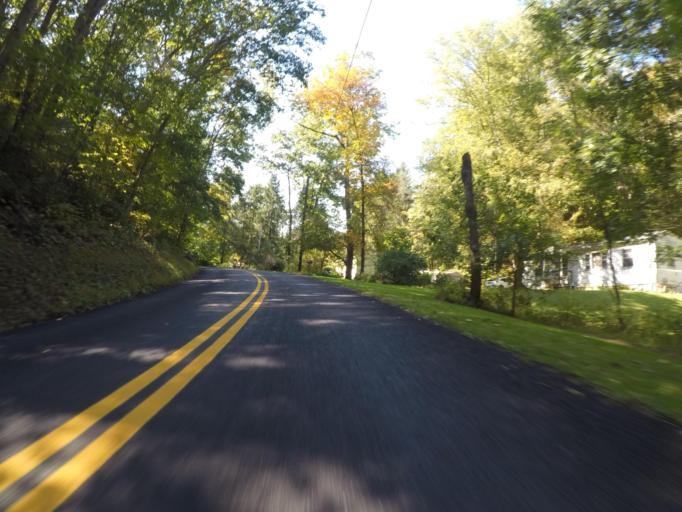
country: US
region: Maryland
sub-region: Carroll County
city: Hampstead
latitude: 39.5878
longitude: -76.9015
